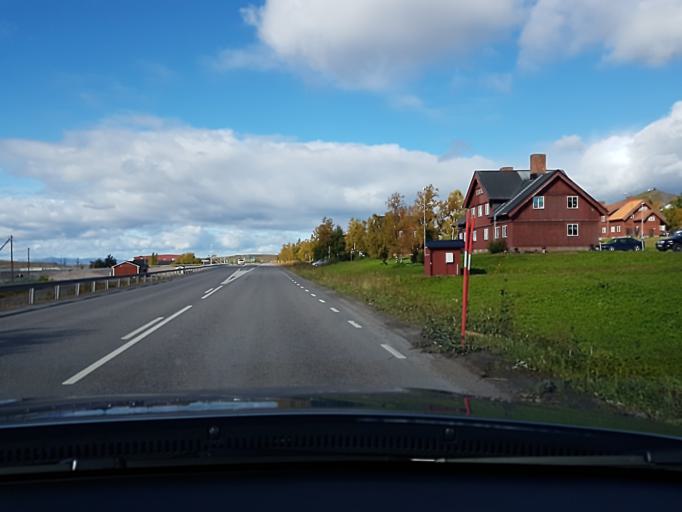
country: SE
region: Norrbotten
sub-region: Kiruna Kommun
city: Kiruna
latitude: 67.8577
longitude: 20.2129
